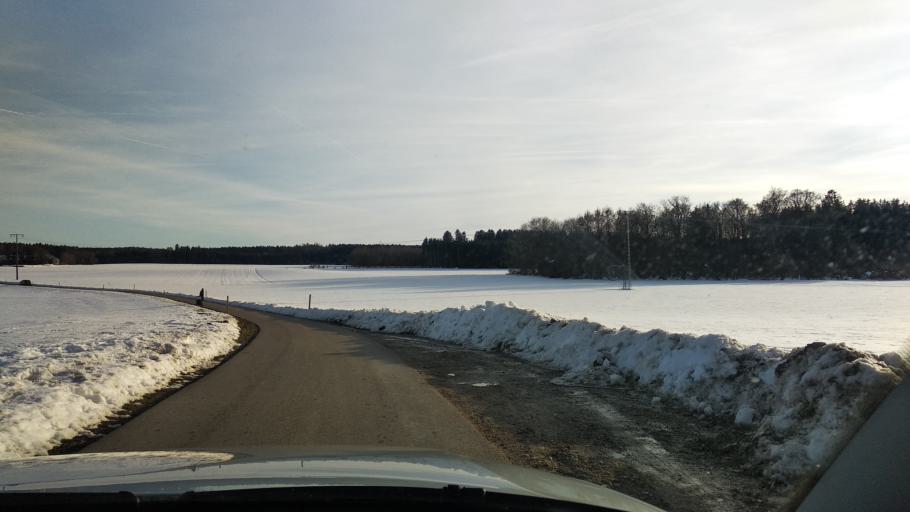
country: DE
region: Bavaria
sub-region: Upper Bavaria
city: Kirchseeon
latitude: 48.0763
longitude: 11.8636
